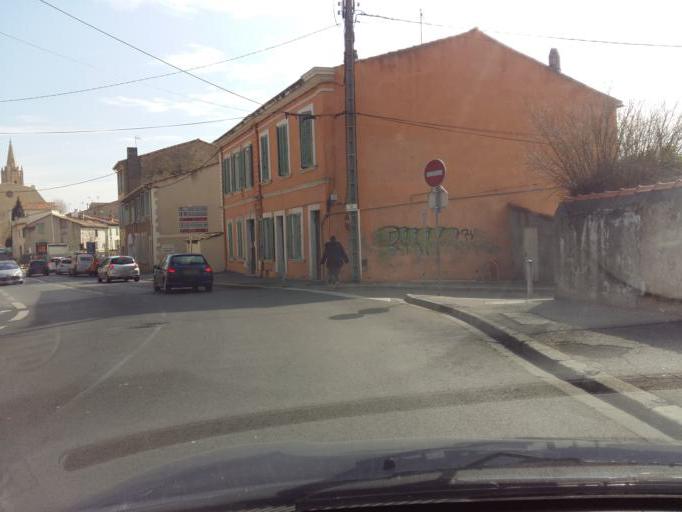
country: FR
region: Provence-Alpes-Cote d'Azur
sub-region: Departement des Bouches-du-Rhone
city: Salon-de-Provence
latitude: 43.6444
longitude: 5.0942
